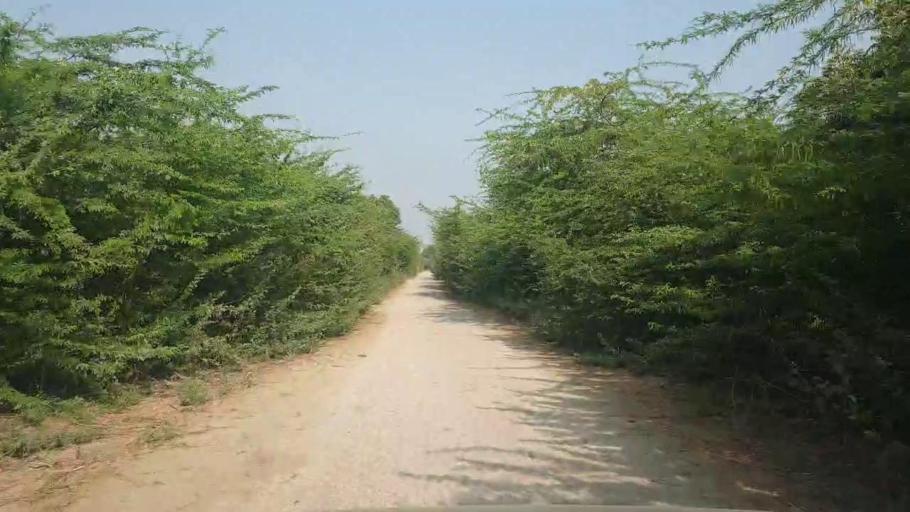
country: PK
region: Sindh
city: Umarkot
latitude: 25.3776
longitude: 69.7296
